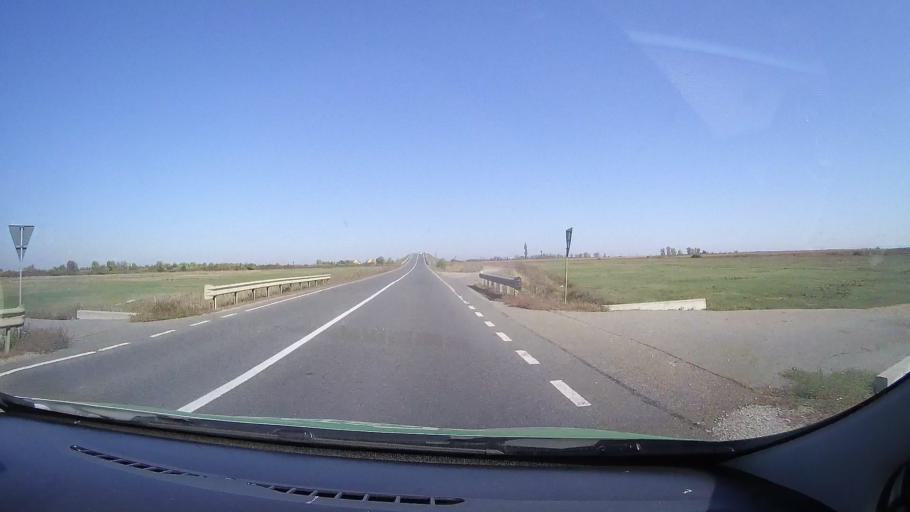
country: RO
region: Satu Mare
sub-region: Comuna Moftinu
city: Moftinu Mic
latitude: 47.6936
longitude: 22.6170
